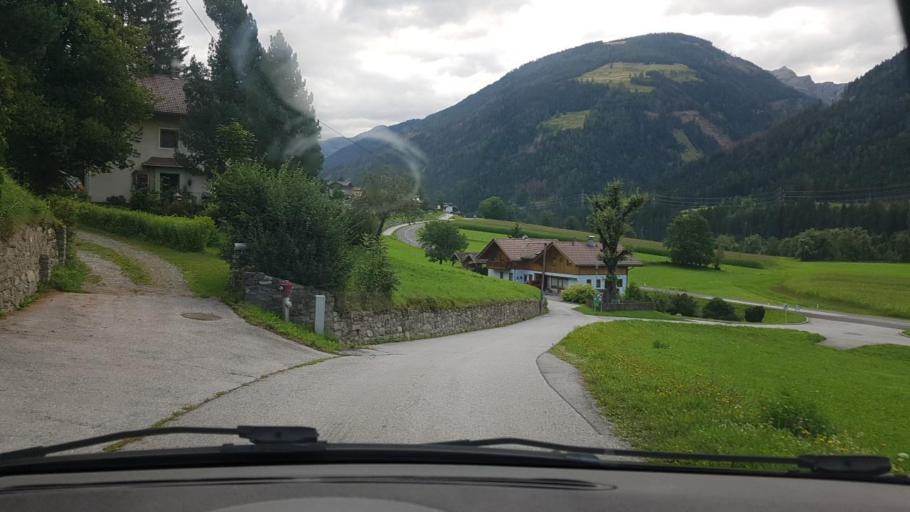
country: AT
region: Carinthia
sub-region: Politischer Bezirk Spittal an der Drau
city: Rangersdorf
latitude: 46.8606
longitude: 12.9532
